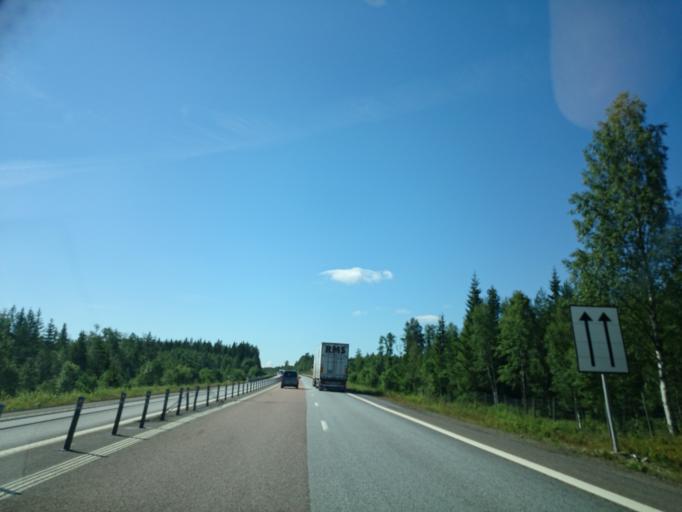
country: SE
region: Gaevleborg
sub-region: Gavle Kommun
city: Norrsundet
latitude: 60.8118
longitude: 17.0826
